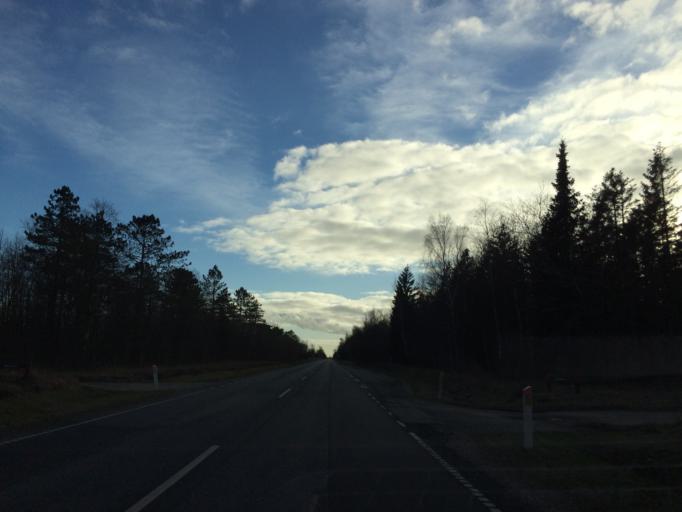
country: DK
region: Central Jutland
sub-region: Lemvig Kommune
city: Lemvig
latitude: 56.4674
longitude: 8.2967
